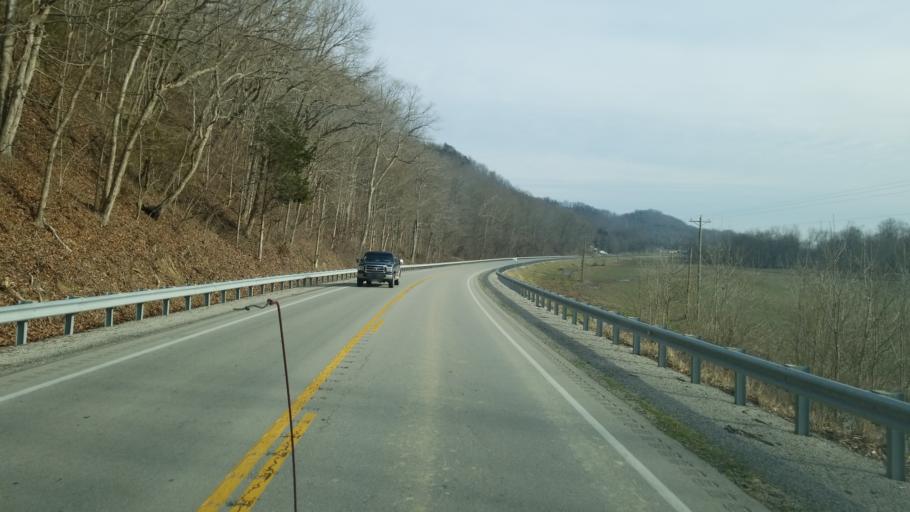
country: US
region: Kentucky
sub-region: Casey County
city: Liberty
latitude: 37.3416
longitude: -84.8984
